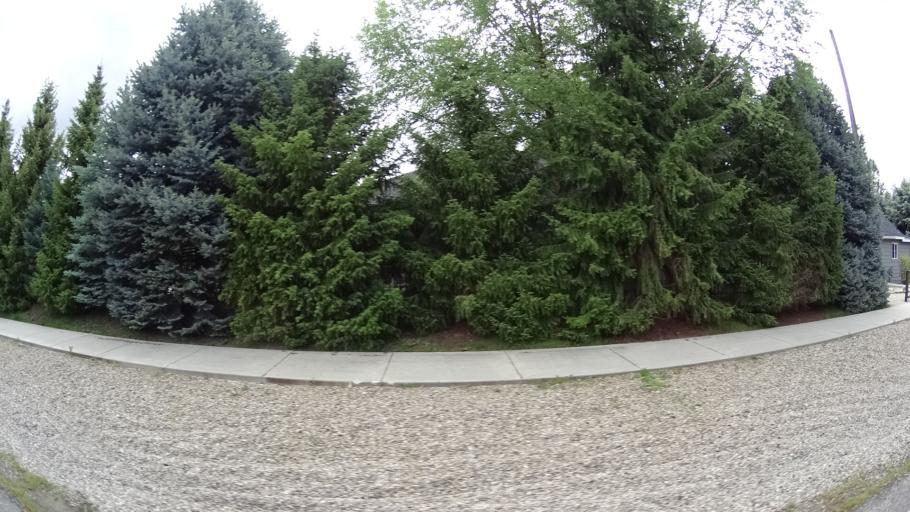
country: US
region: Idaho
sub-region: Ada County
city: Eagle
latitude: 43.6740
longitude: -116.2991
